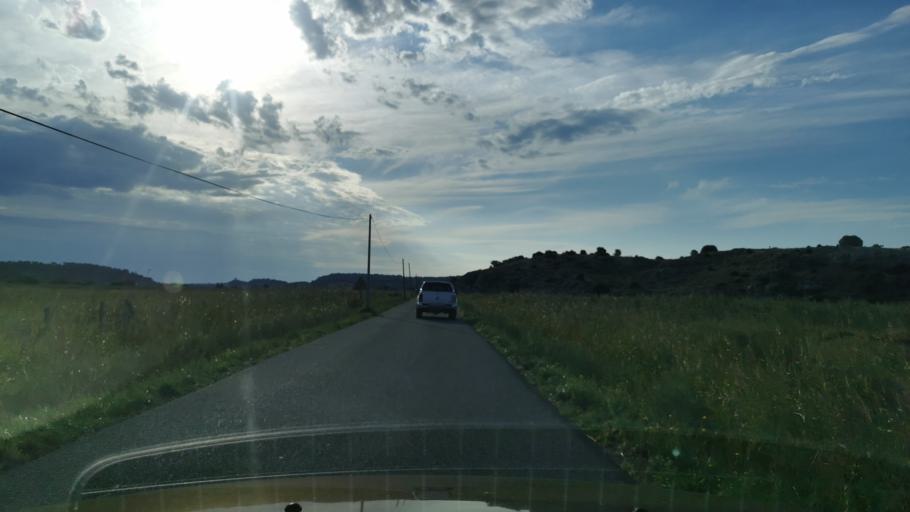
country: FR
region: Languedoc-Roussillon
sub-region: Departement de l'Aude
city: Gruissan
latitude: 43.1147
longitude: 3.0413
